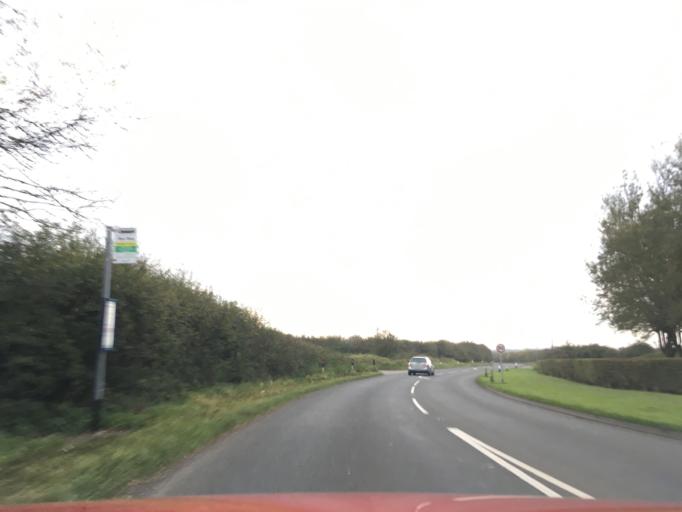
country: GB
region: England
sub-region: South Gloucestershire
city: Pucklechurch
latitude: 51.5038
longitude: -2.4279
